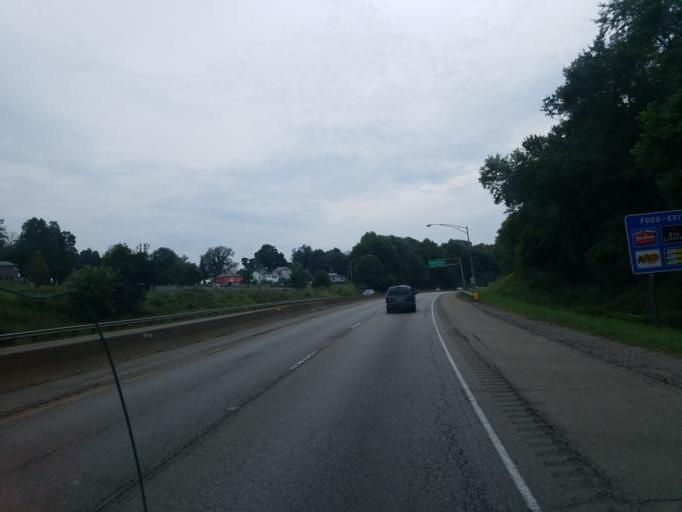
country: US
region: Ohio
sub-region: Muskingum County
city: Zanesville
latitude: 39.9447
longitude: -81.9875
